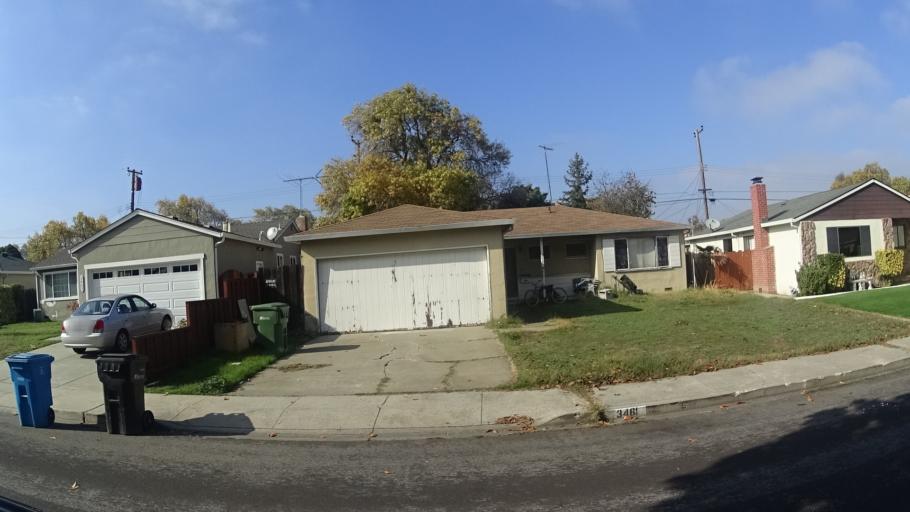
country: US
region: California
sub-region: Santa Clara County
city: Santa Clara
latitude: 37.3558
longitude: -121.9915
